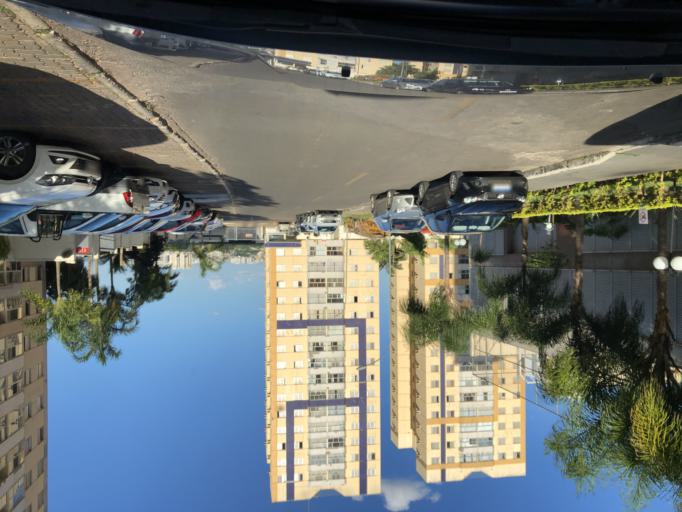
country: BR
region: Federal District
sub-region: Brasilia
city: Brasilia
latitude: -15.8382
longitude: -48.0111
